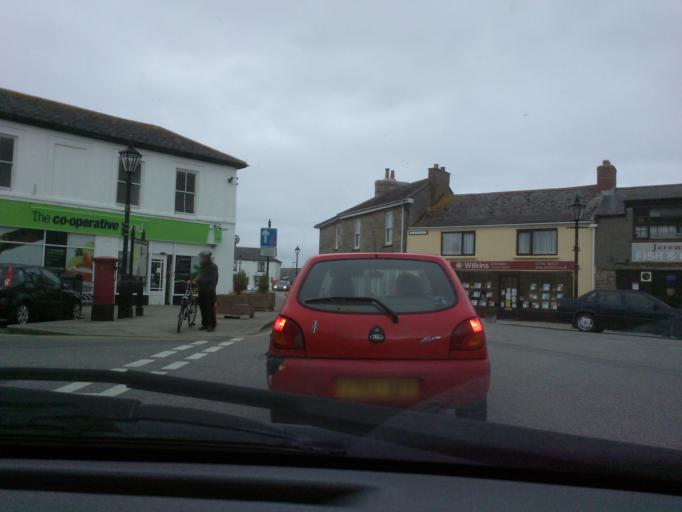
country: GB
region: England
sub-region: Cornwall
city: Saint Just
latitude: 50.1243
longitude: -5.6798
